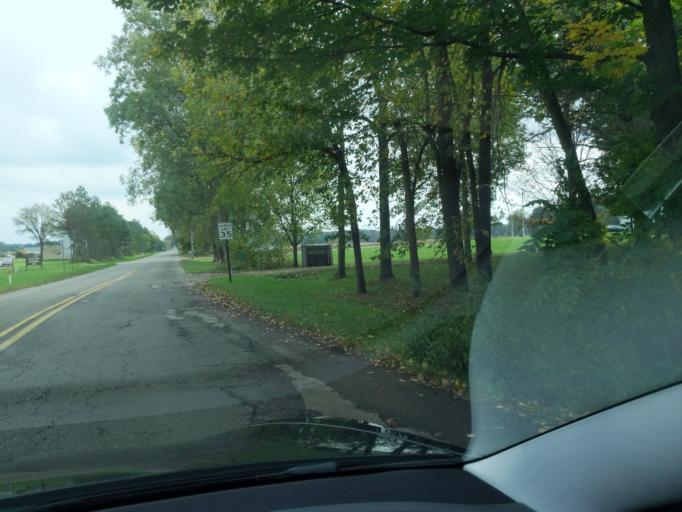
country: US
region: Michigan
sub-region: Eaton County
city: Eaton Rapids
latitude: 42.4943
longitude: -84.6565
